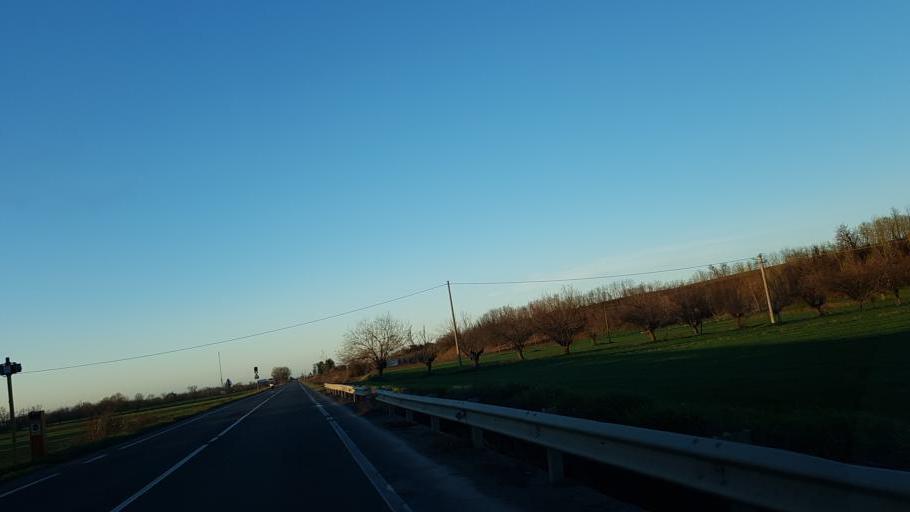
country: IT
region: Piedmont
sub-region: Provincia di Alessandria
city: Villalvernia
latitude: 44.8295
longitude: 8.8540
